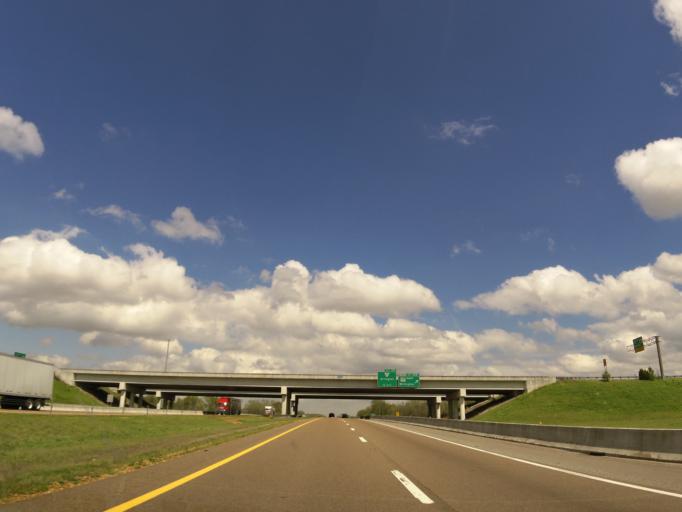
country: US
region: Tennessee
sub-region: Shelby County
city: Arlington
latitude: 35.2552
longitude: -89.6784
